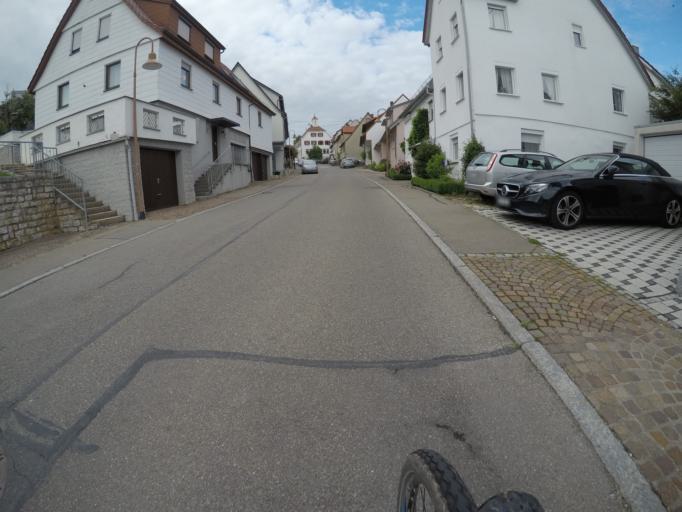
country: DE
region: Baden-Wuerttemberg
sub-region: Regierungsbezirk Stuttgart
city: Grossbettlingen
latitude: 48.5685
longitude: 9.3060
